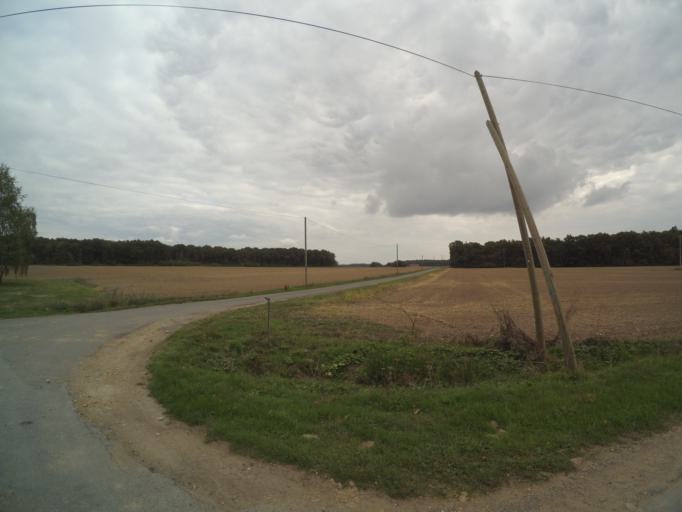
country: FR
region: Centre
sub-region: Departement d'Indre-et-Loire
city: Auzouer-en-Touraine
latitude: 47.5176
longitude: 0.9802
